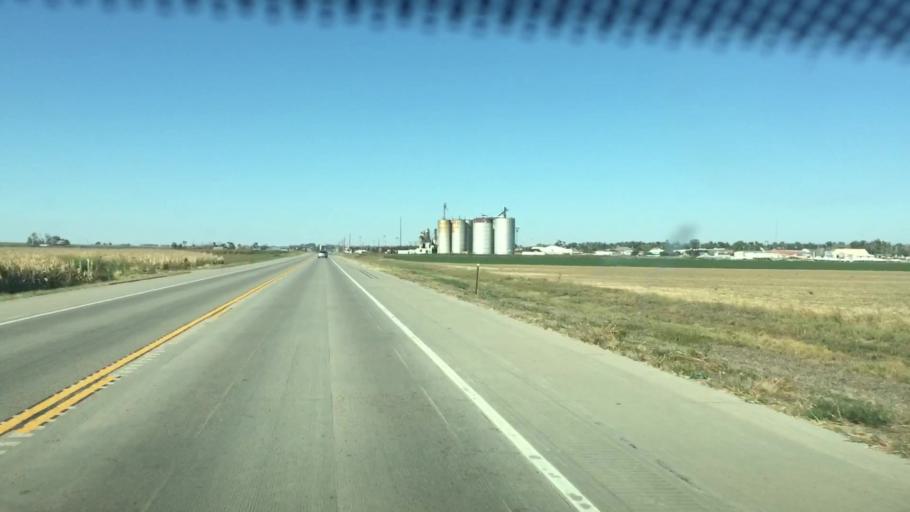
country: US
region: Colorado
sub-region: Prowers County
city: Lamar
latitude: 38.1461
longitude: -102.7237
